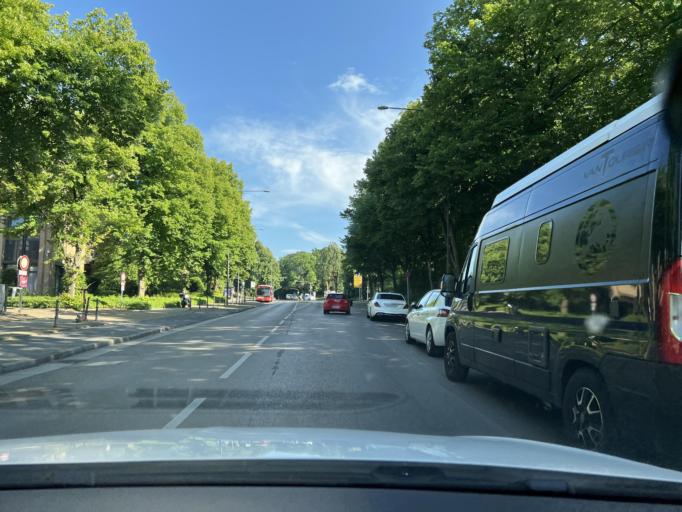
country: DE
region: North Rhine-Westphalia
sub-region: Regierungsbezirk Koln
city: Aachen
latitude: 50.7535
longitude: 6.0971
